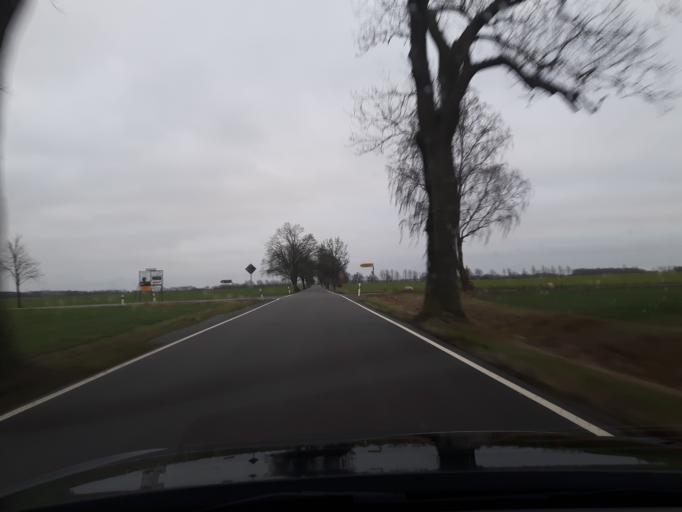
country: DE
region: Mecklenburg-Vorpommern
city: Bad Sulze
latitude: 54.0527
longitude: 12.6732
